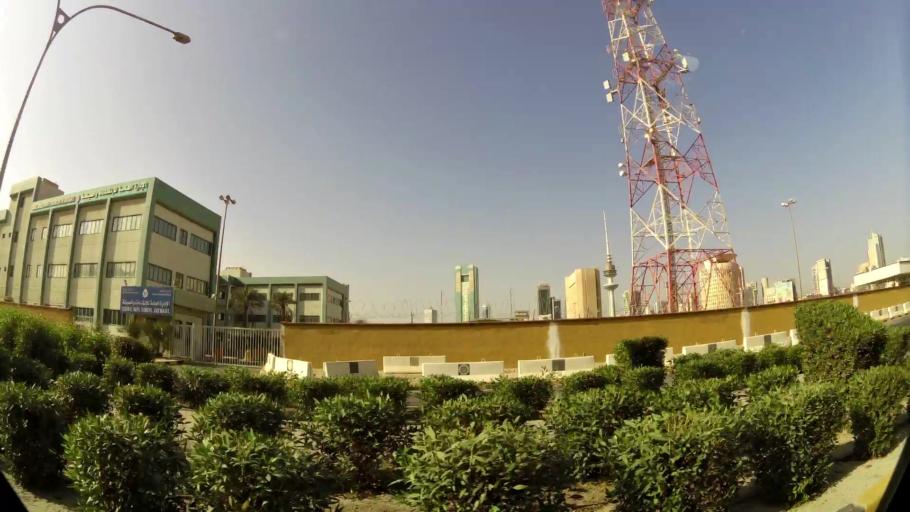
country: KW
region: Al Asimah
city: Kuwait City
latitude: 29.3727
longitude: 47.9865
